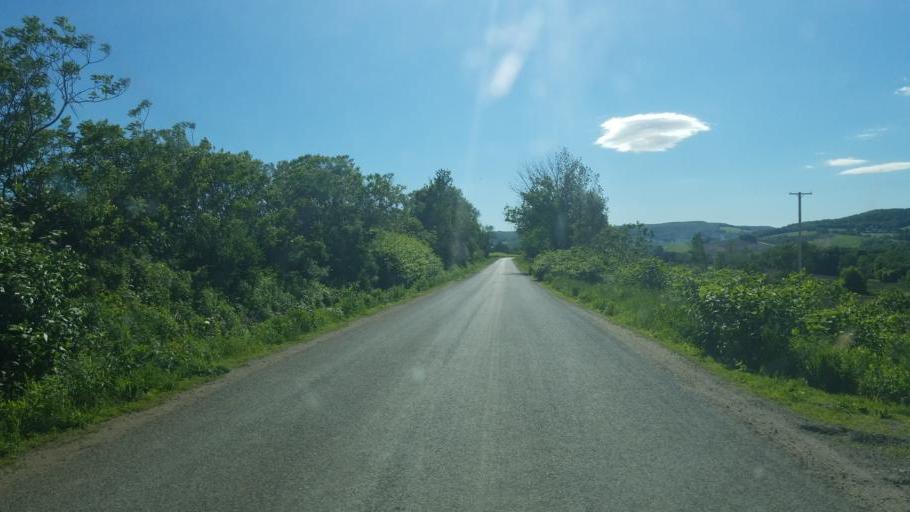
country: US
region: New York
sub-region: Herkimer County
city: Little Falls
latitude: 42.9765
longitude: -74.7989
